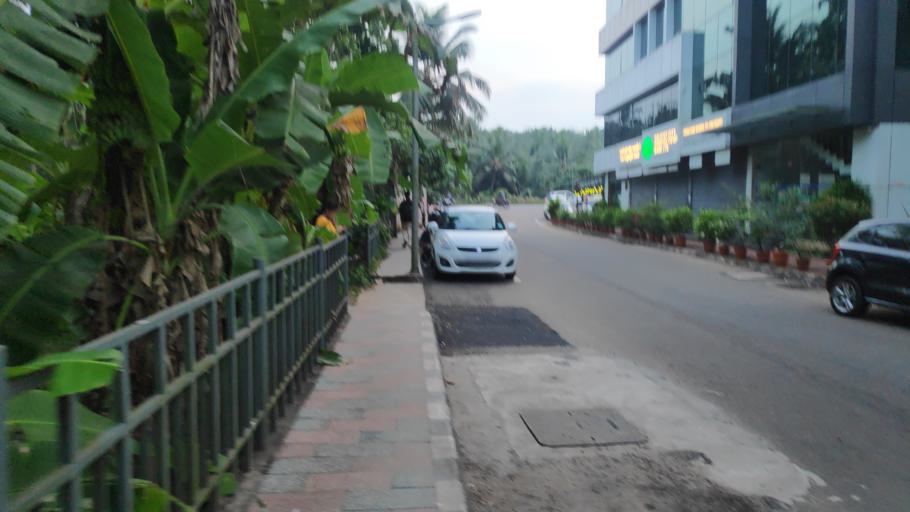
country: IN
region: Kerala
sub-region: Kozhikode
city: Kozhikode
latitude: 11.2536
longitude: 75.8275
